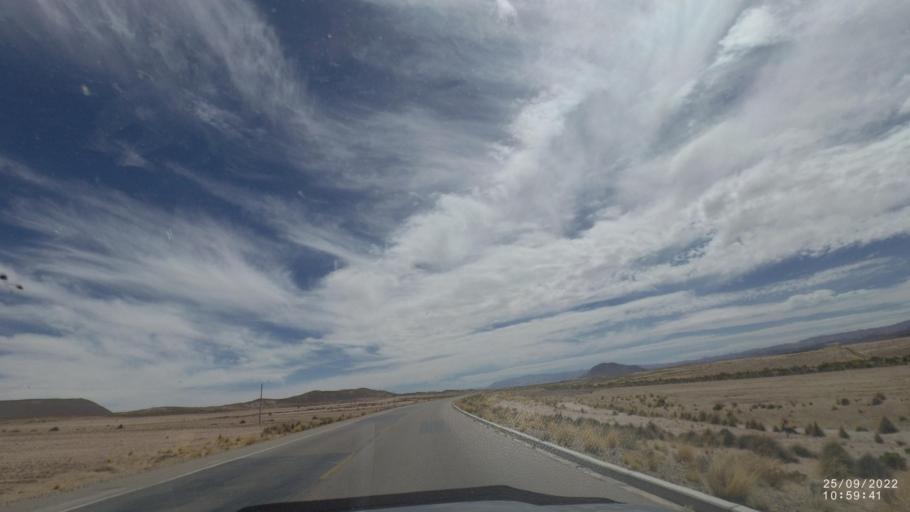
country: BO
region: Oruro
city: Challapata
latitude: -19.4444
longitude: -66.9097
